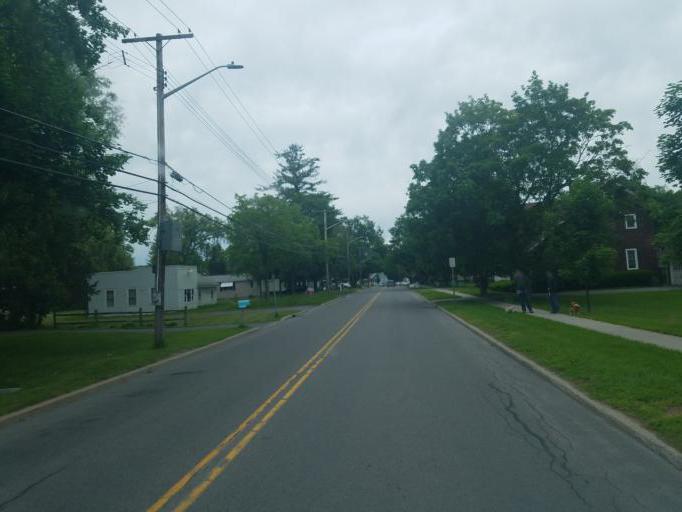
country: US
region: New York
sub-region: Herkimer County
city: Ilion
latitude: 43.0011
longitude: -75.0464
